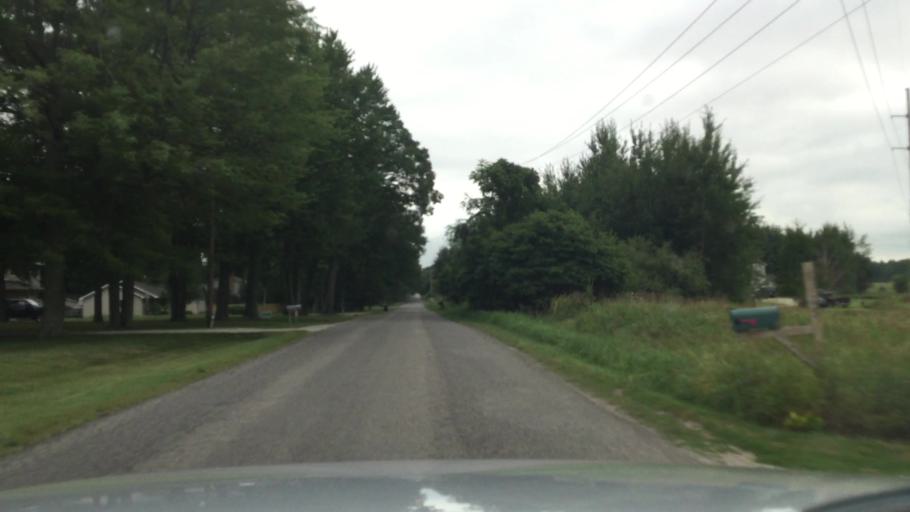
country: US
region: Michigan
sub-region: Montcalm County
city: Greenville
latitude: 43.1757
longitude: -85.2234
